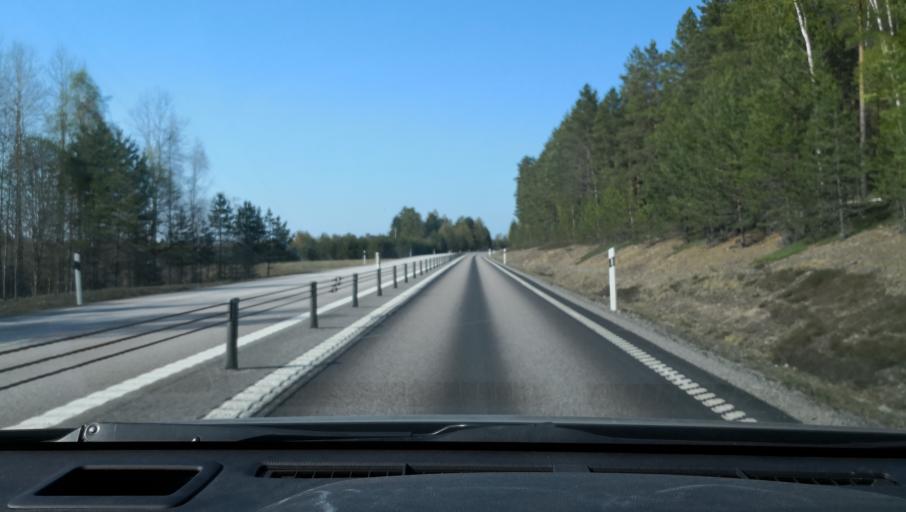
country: SE
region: Uppsala
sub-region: Heby Kommun
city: Tarnsjo
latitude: 60.2174
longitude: 16.9519
